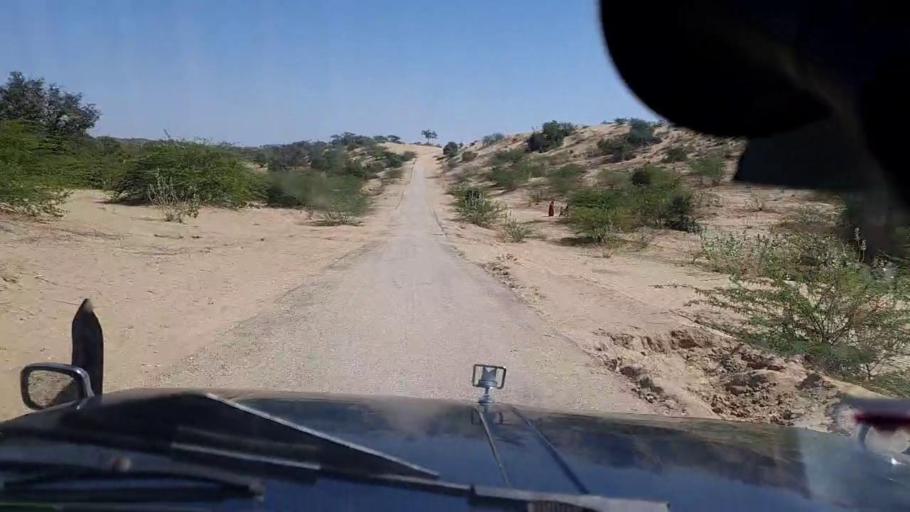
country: PK
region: Sindh
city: Diplo
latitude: 24.5615
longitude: 69.6794
